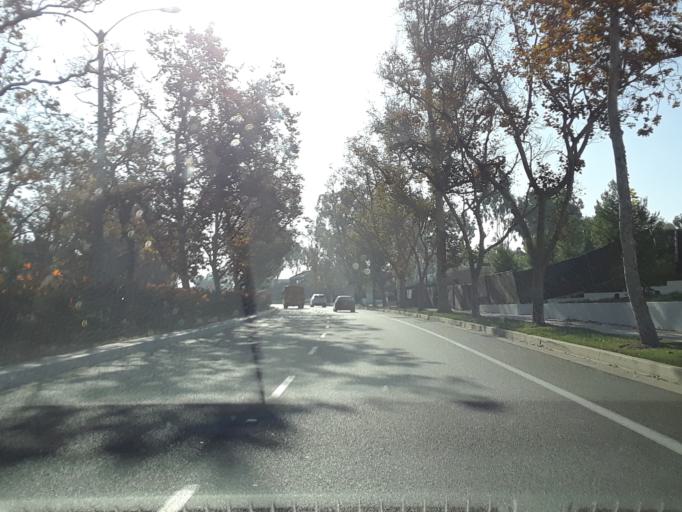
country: US
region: California
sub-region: Orange County
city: Irvine
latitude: 33.6774
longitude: -117.7984
